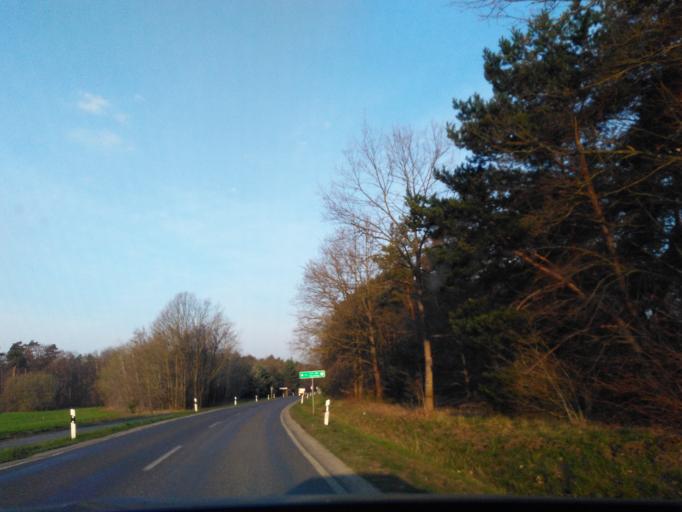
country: DE
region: Brandenburg
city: Strausberg
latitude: 52.5668
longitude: 13.9365
